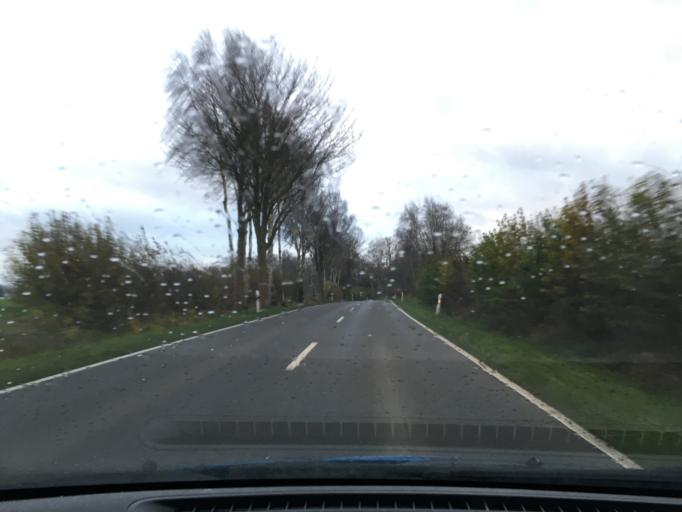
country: DE
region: Lower Saxony
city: Hermannsburg
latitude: 52.8202
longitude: 10.0581
